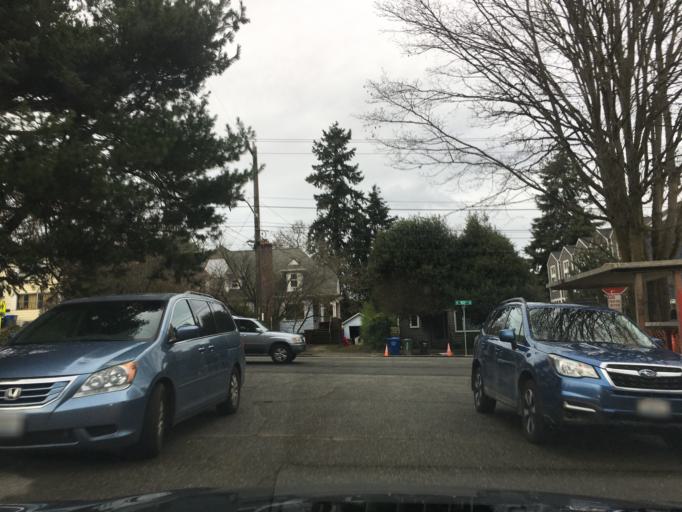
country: US
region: Washington
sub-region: King County
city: Seattle
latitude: 47.6648
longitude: -122.3291
